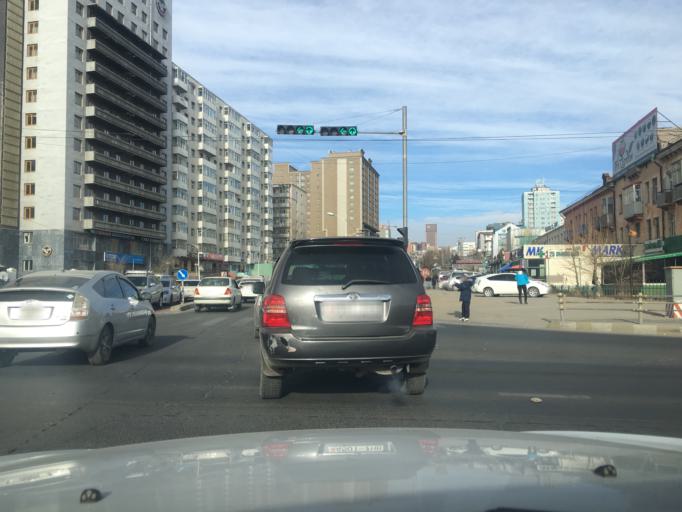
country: MN
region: Ulaanbaatar
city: Ulaanbaatar
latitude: 47.9144
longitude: 106.8769
